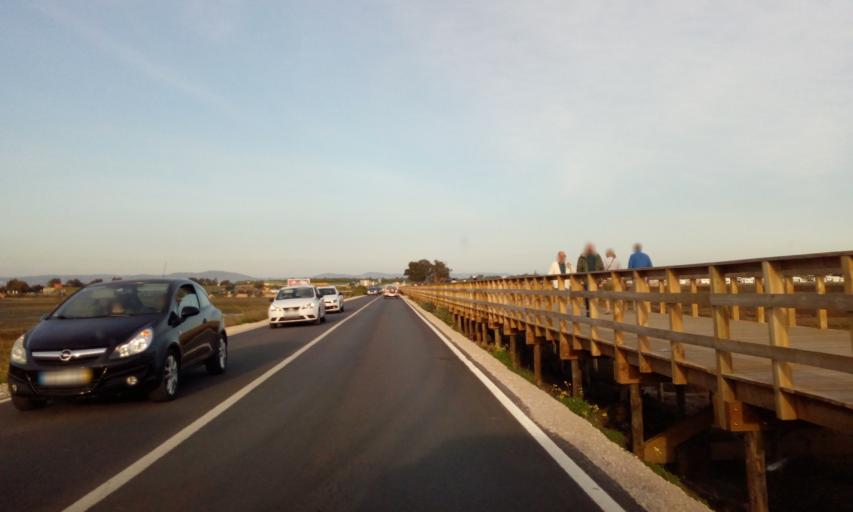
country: PT
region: Faro
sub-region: Faro
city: Faro
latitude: 37.0128
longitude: -7.9897
